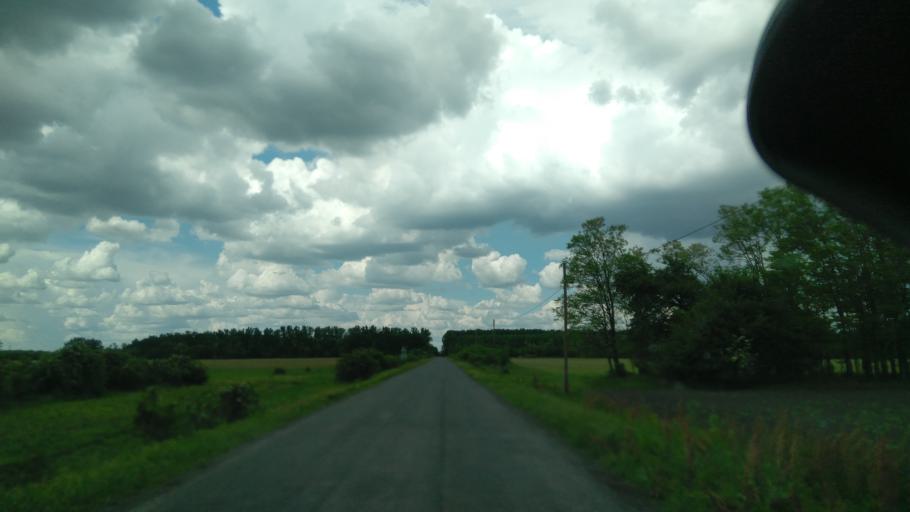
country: HU
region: Bekes
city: Szeghalom
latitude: 47.1116
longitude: 21.0878
